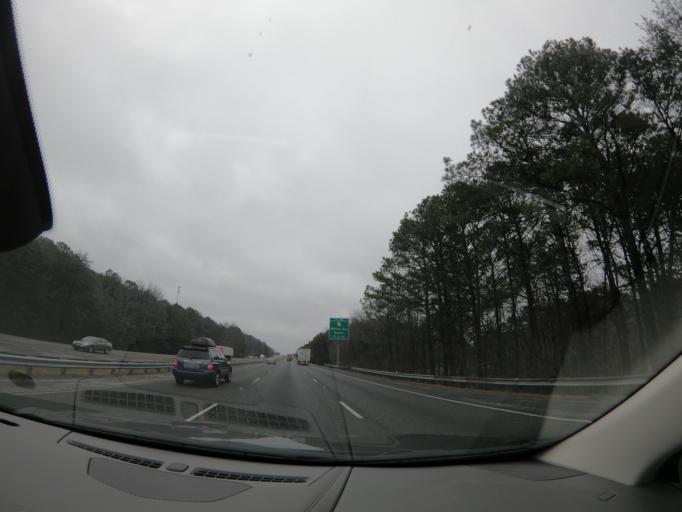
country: US
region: Georgia
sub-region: Whitfield County
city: Dalton
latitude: 34.7507
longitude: -85.0024
